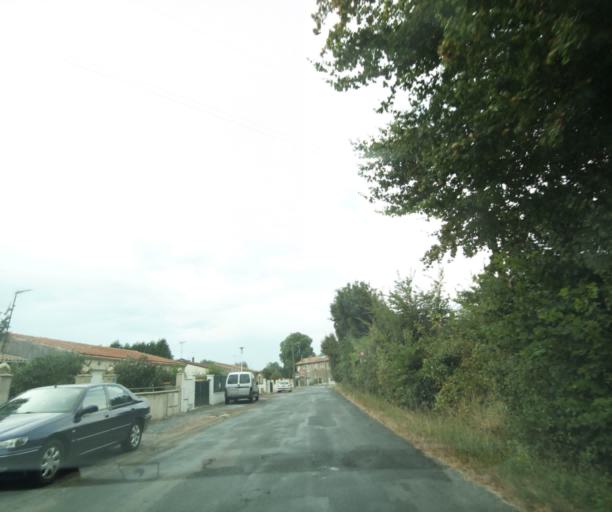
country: FR
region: Poitou-Charentes
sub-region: Departement de la Charente-Maritime
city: Tonnay-Charente
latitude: 45.9491
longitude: -0.9272
